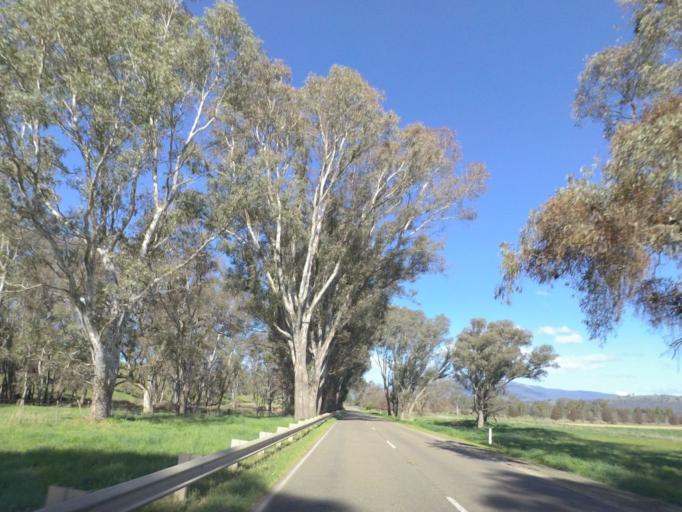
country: AU
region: Victoria
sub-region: Murrindindi
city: Alexandra
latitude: -37.2303
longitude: 145.7649
